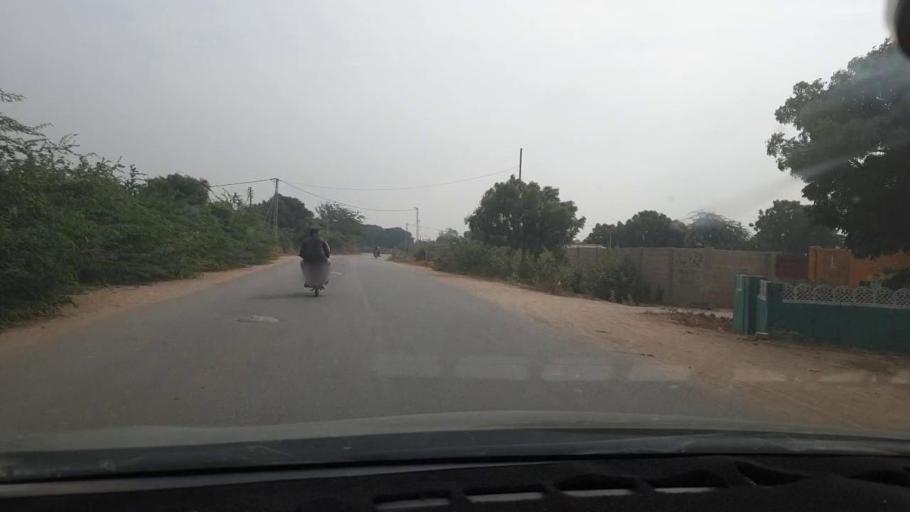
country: PK
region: Sindh
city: Malir Cantonment
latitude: 24.9153
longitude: 67.2609
